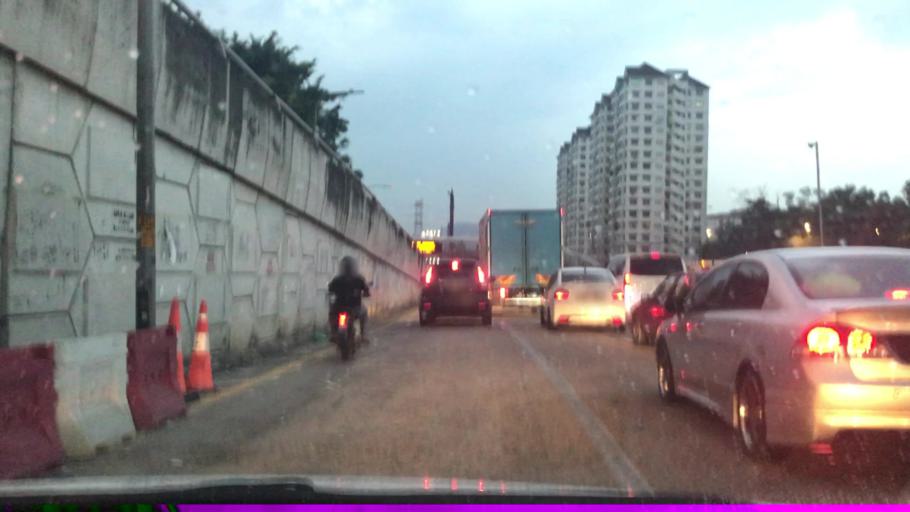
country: MY
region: Selangor
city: Kampong Baharu Balakong
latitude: 3.0771
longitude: 101.7154
